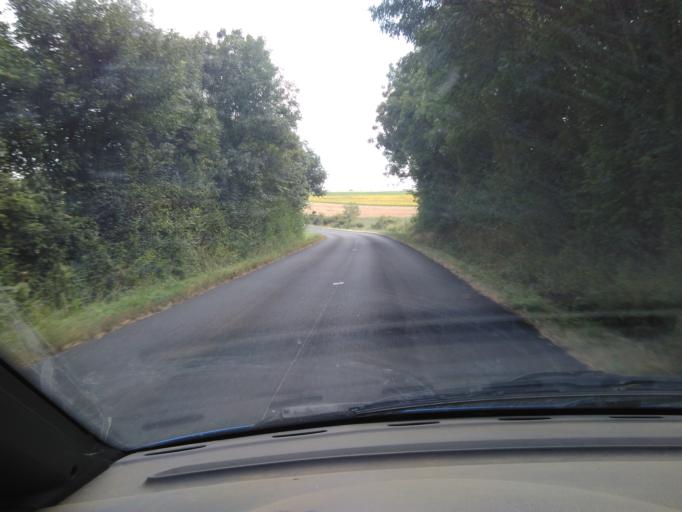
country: FR
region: Pays de la Loire
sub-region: Departement de la Vendee
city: Sainte-Hermine
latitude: 46.5540
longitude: -1.0337
